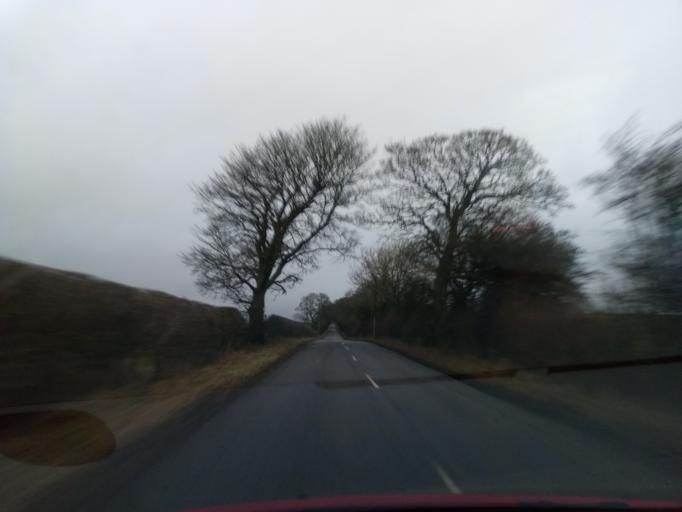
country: GB
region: England
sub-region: Northumberland
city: Rothley
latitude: 55.1894
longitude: -1.9705
